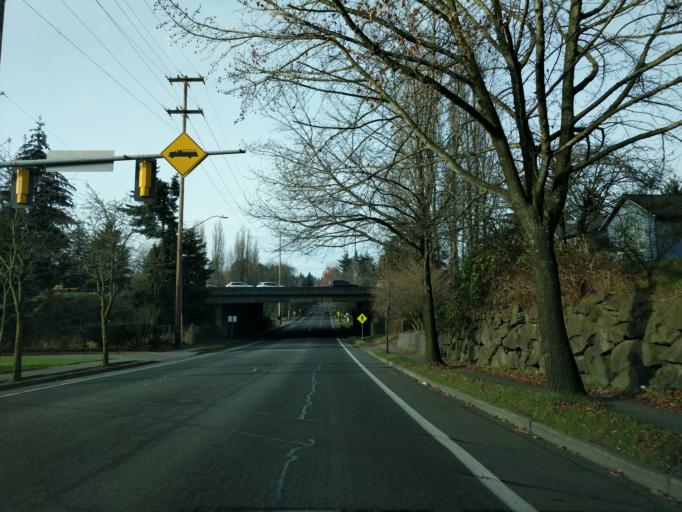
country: US
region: Washington
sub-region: King County
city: Shoreline
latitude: 47.7415
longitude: -122.3279
